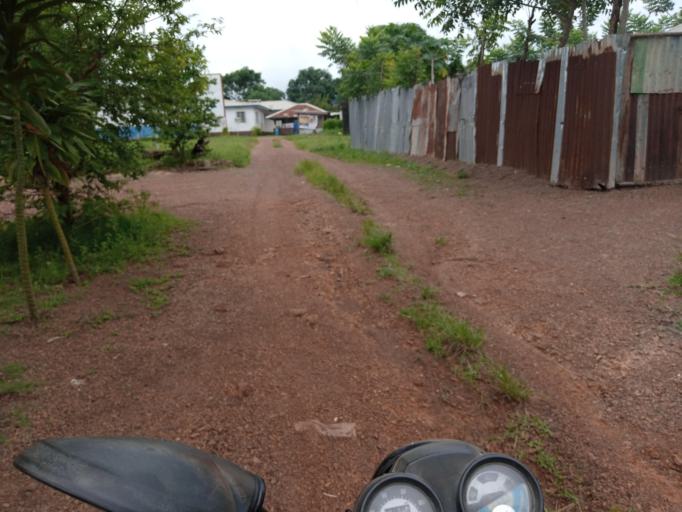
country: SL
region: Southern Province
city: Largo
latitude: 8.1937
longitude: -12.0619
